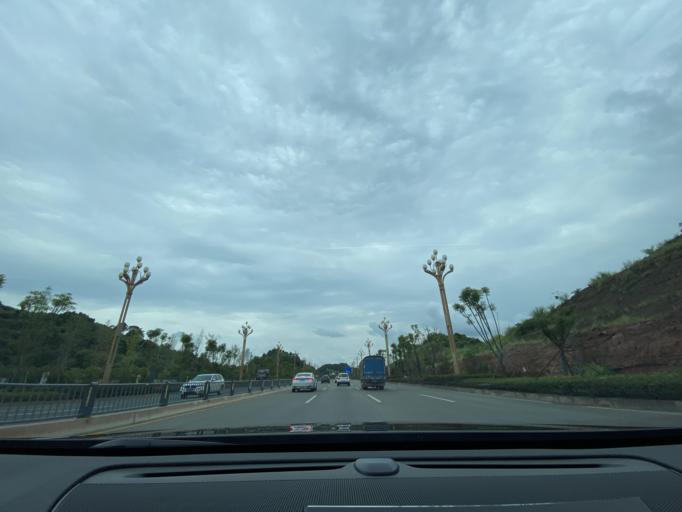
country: CN
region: Sichuan
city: Jiancheng
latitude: 30.4746
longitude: 104.4901
